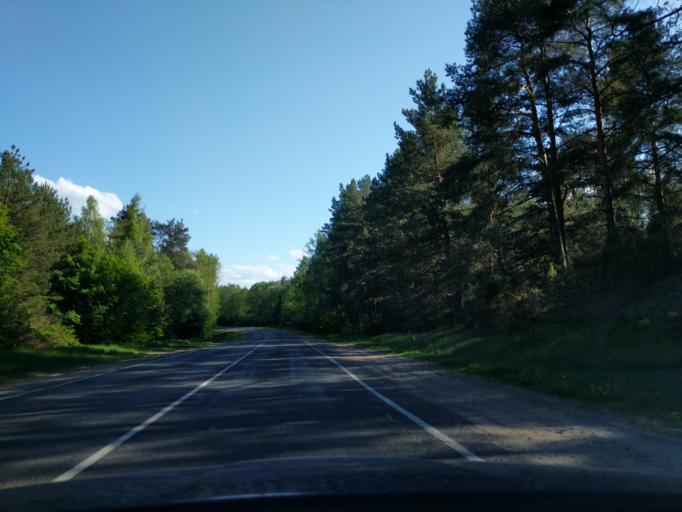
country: BY
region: Minsk
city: Myadzyel
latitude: 54.8454
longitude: 26.9260
